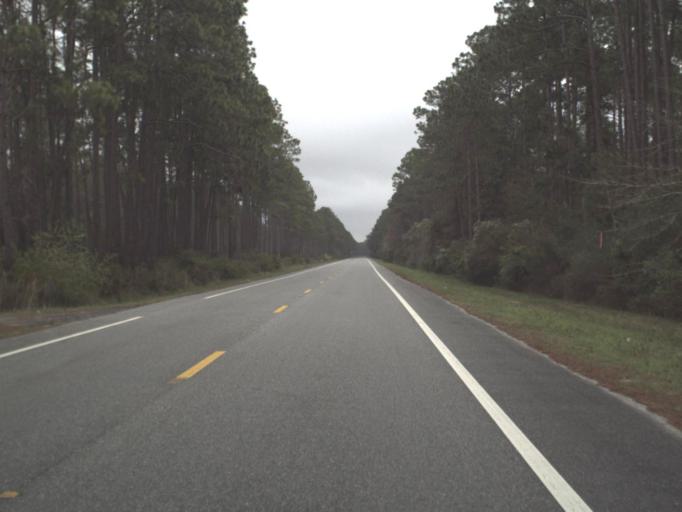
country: US
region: Florida
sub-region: Franklin County
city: Eastpoint
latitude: 29.8290
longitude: -84.8766
